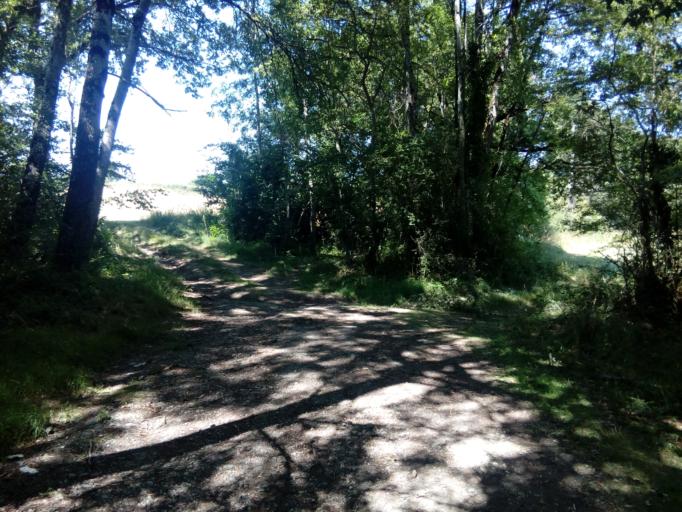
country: FR
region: Limousin
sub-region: Departement de la Creuse
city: Gueret
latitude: 46.2040
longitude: 1.8864
